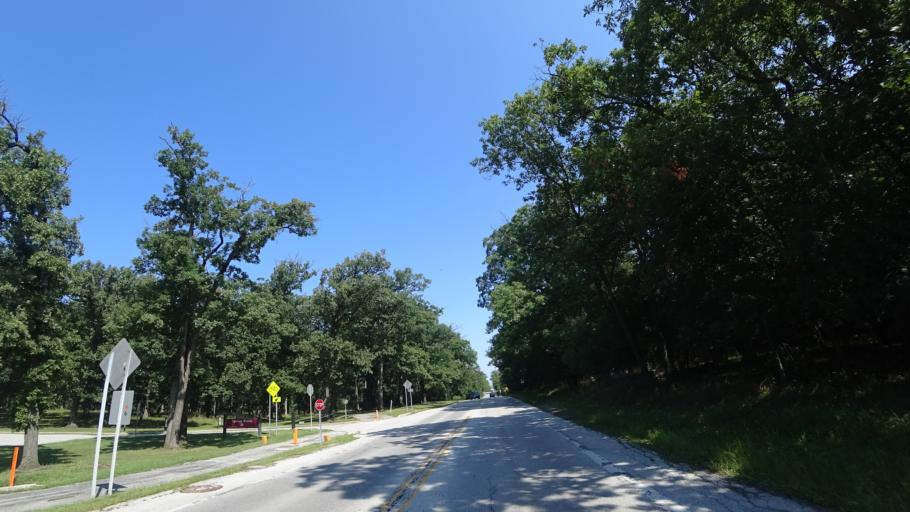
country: US
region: Illinois
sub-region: Cook County
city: Oak Forest
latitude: 41.5925
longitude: -87.7556
